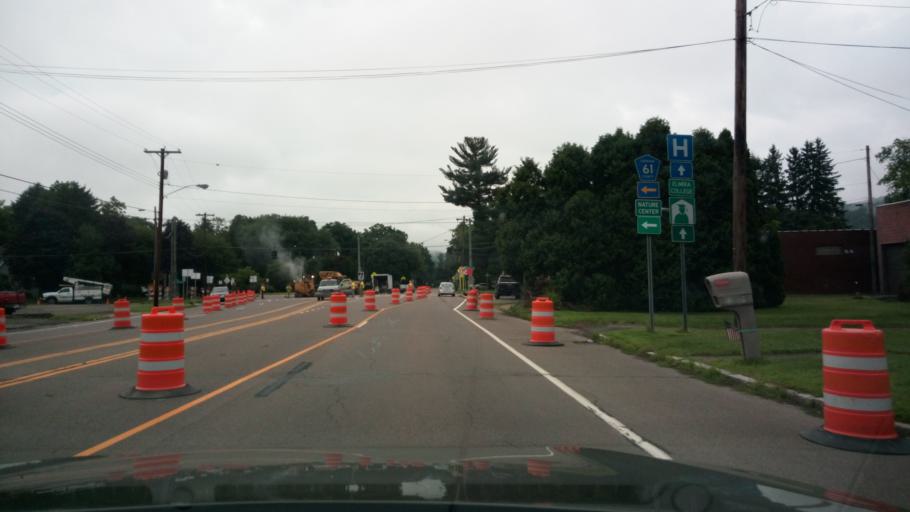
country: US
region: New York
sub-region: Chemung County
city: West Elmira
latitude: 42.0813
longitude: -76.8581
